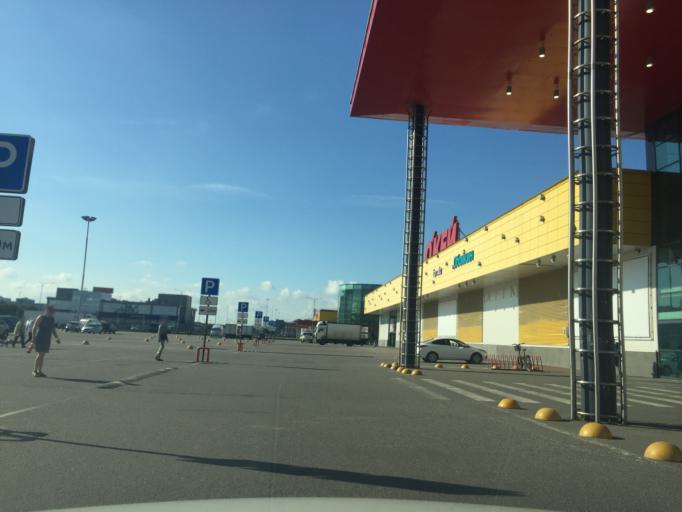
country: RU
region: St.-Petersburg
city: Kupchino
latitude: 59.8281
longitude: 30.3173
